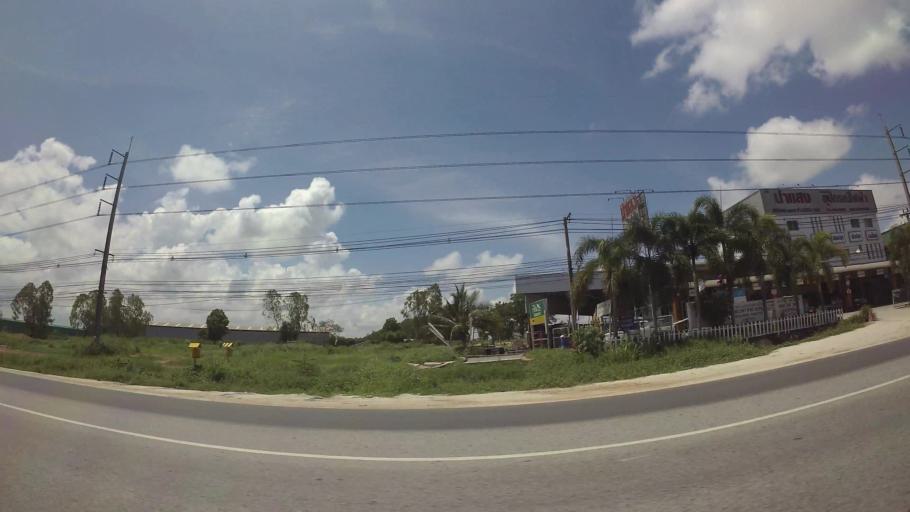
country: TH
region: Rayong
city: Rayong
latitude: 12.7198
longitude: 101.2238
